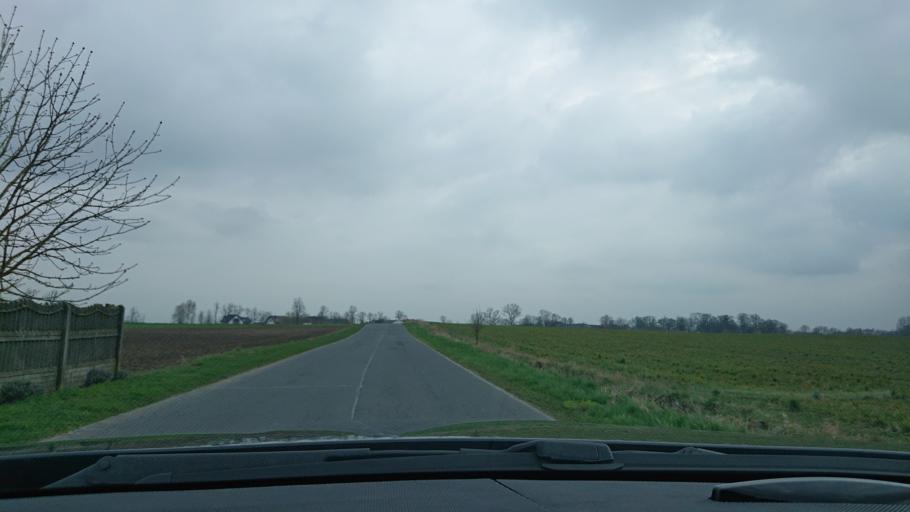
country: PL
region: Greater Poland Voivodeship
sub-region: Powiat gnieznienski
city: Lubowo
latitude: 52.5354
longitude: 17.4937
